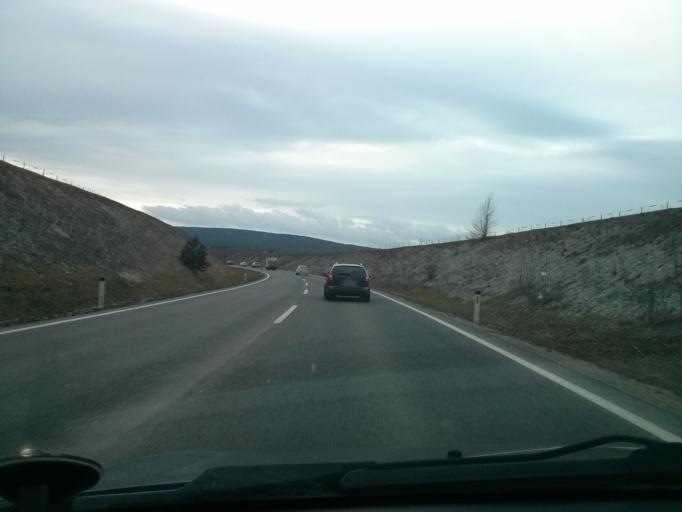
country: AT
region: Lower Austria
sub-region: Politischer Bezirk Wiener Neustadt
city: Theresienfeld
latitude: 47.8527
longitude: 16.2155
